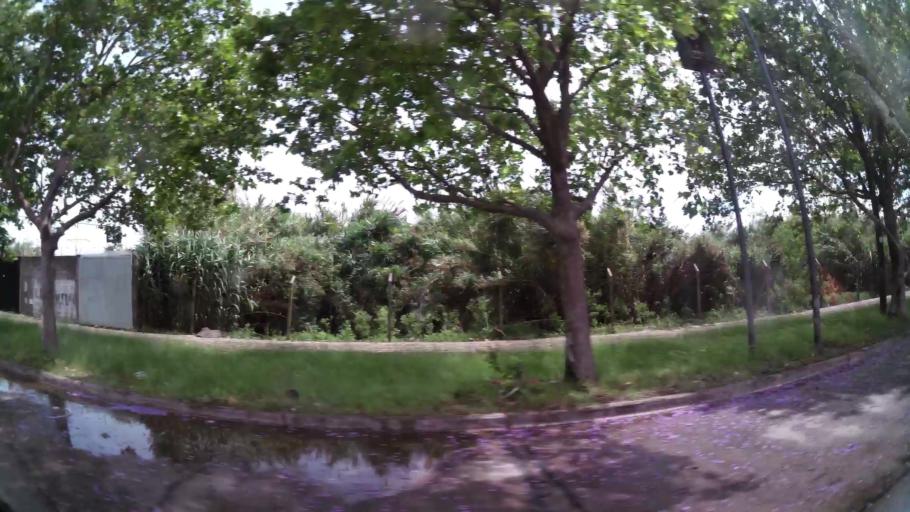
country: AR
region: Buenos Aires F.D.
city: Villa Lugano
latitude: -34.6840
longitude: -58.4455
